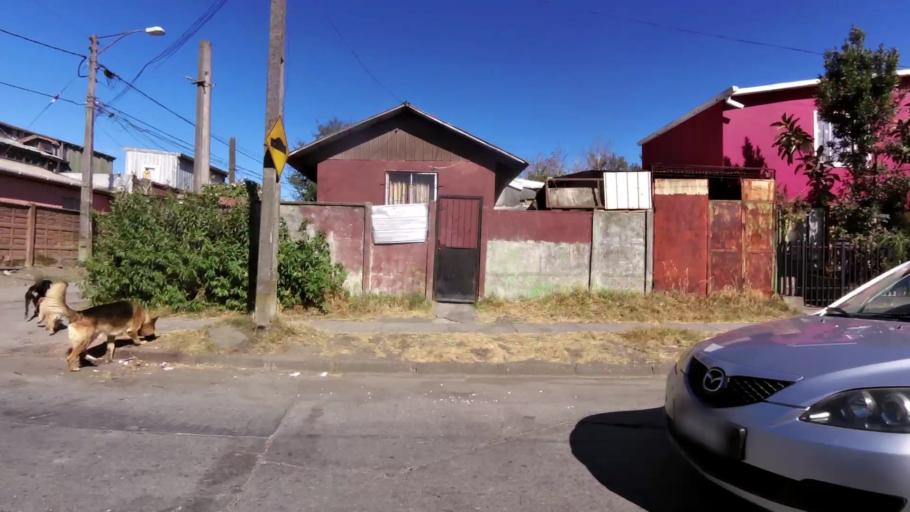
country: CL
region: Biobio
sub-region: Provincia de Concepcion
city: Concepcion
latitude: -36.8154
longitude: -73.0776
